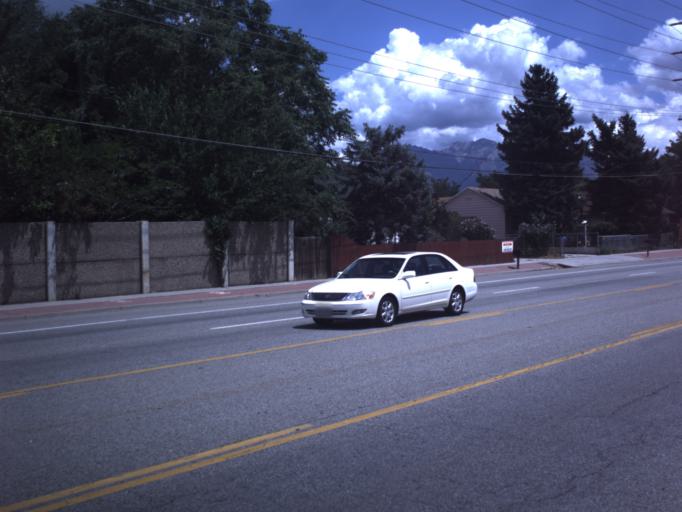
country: US
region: Utah
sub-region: Salt Lake County
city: South Jordan
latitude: 40.5877
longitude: -111.9234
